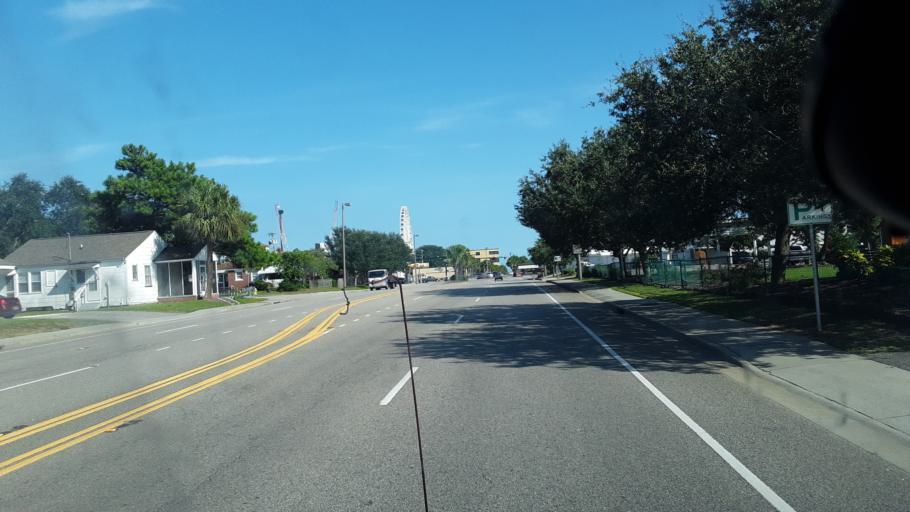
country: US
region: South Carolina
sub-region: Horry County
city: Myrtle Beach
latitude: 33.6967
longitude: -78.8818
